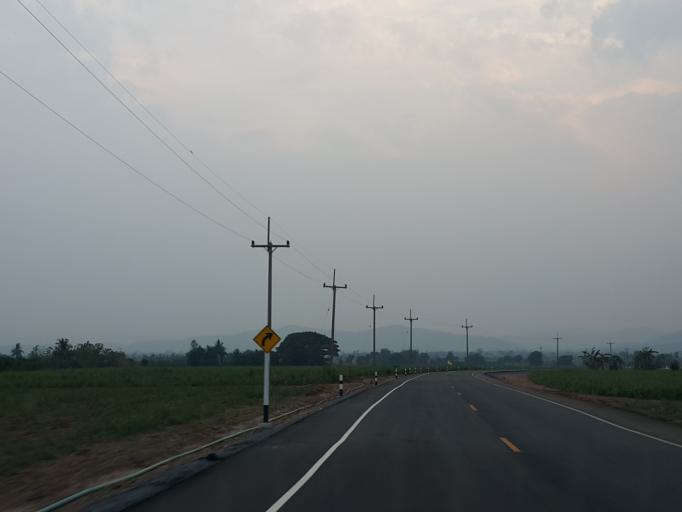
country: TH
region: Suphan Buri
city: Dan Chang
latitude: 14.9400
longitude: 99.6454
